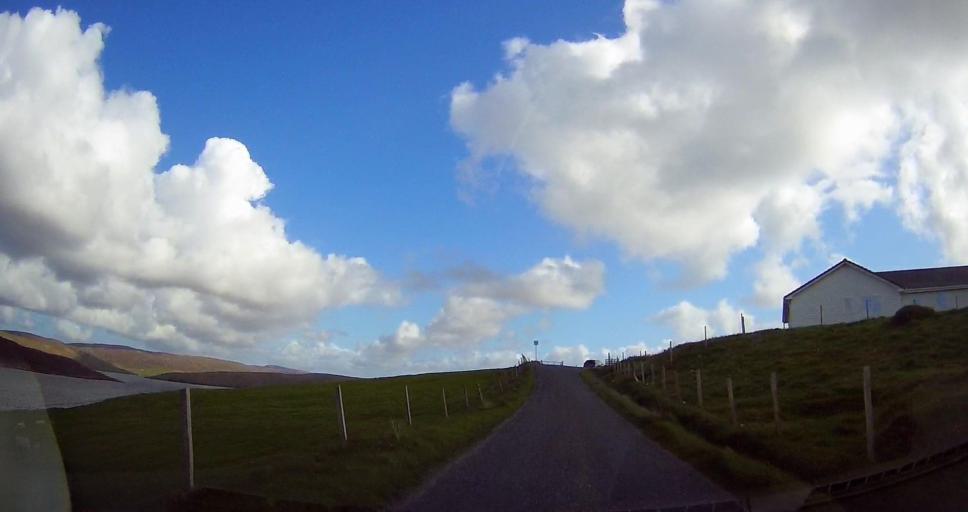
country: GB
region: Scotland
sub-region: Shetland Islands
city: Lerwick
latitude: 60.3612
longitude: -1.3836
